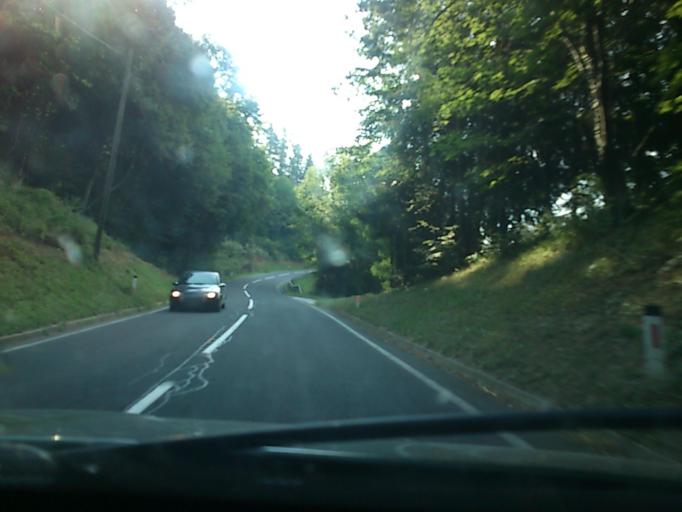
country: SI
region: Starse
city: Starse
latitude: 46.4947
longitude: 15.7906
